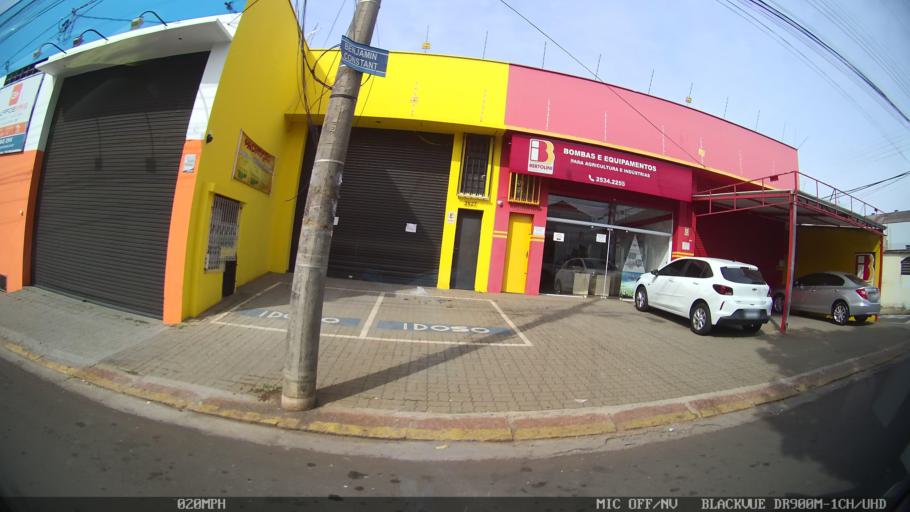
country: BR
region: Sao Paulo
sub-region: Piracicaba
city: Piracicaba
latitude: -22.7414
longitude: -47.6545
